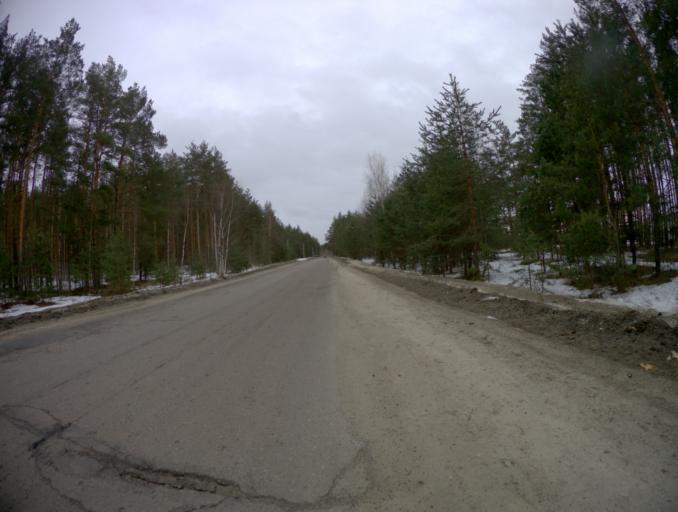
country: RU
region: Vladimir
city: Kommunar
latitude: 56.1366
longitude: 40.4905
